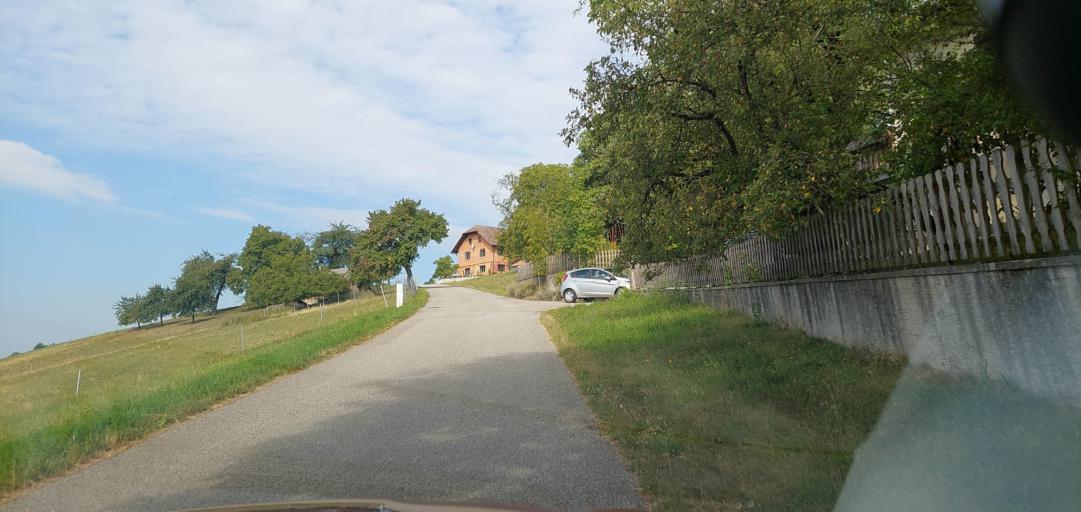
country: AT
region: Upper Austria
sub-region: Politischer Bezirk Urfahr-Umgebung
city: Feldkirchen an der Donau
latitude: 48.3310
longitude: 13.9844
